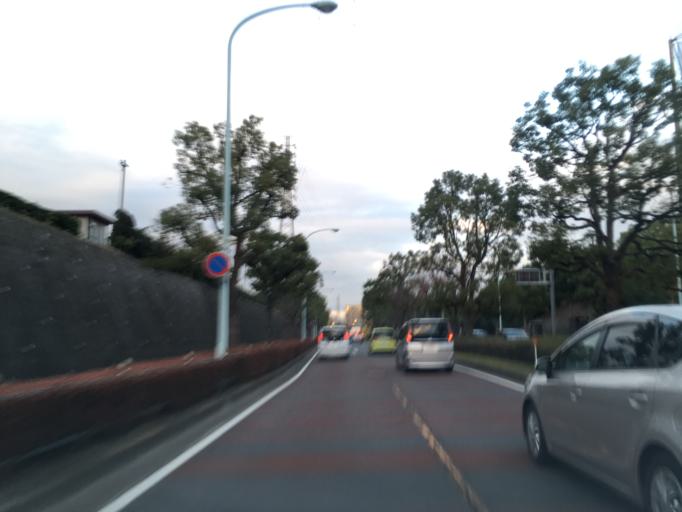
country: JP
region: Tokyo
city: Hachioji
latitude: 35.6077
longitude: 139.3704
